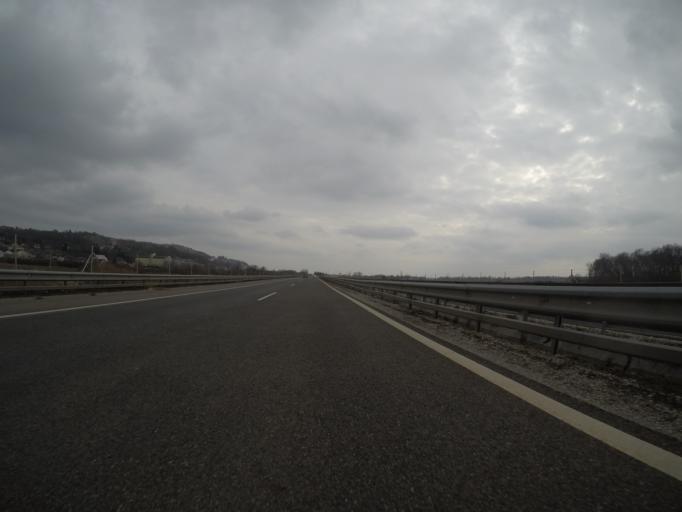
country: SI
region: Lendava-Lendva
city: Lendava
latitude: 46.5744
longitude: 16.4415
